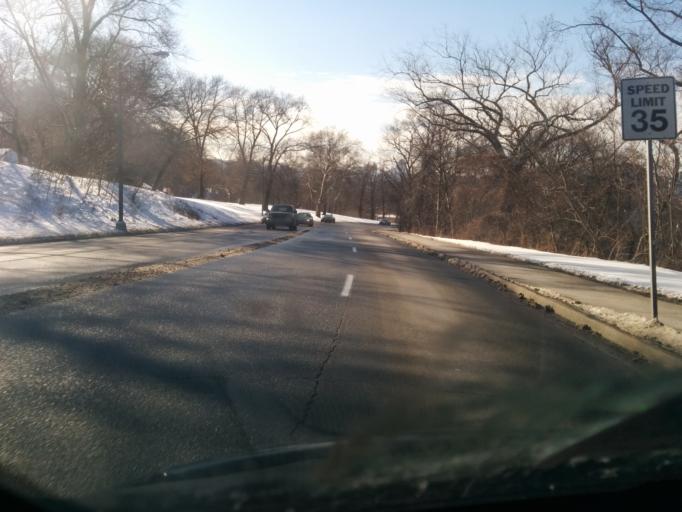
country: US
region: Pennsylvania
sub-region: Allegheny County
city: Bloomfield
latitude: 40.4346
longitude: -79.9426
